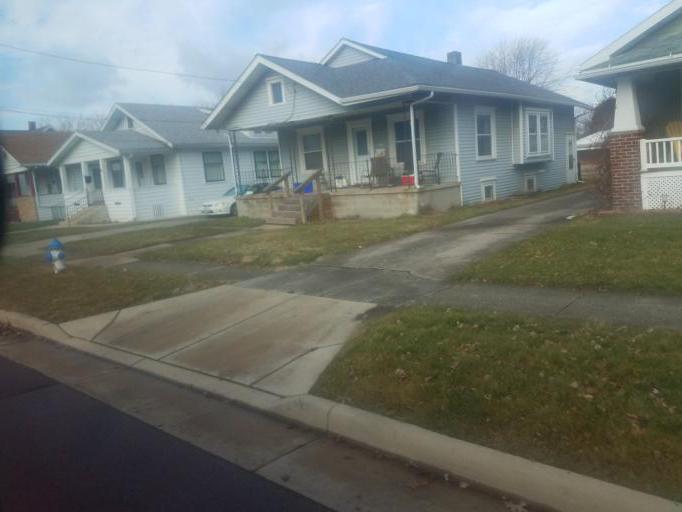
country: US
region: Ohio
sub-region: Marion County
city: Marion
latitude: 40.5763
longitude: -83.1476
